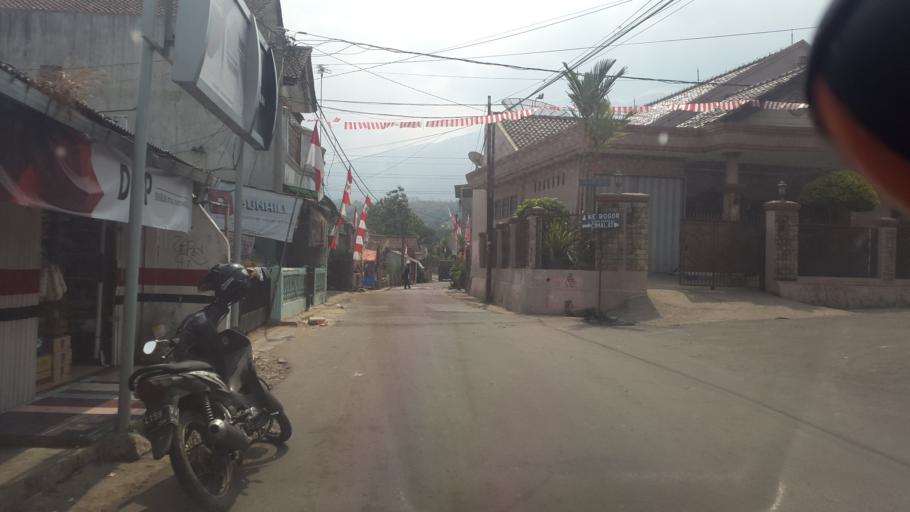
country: ID
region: West Java
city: Cicurug
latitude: -6.7661
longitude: 106.7733
